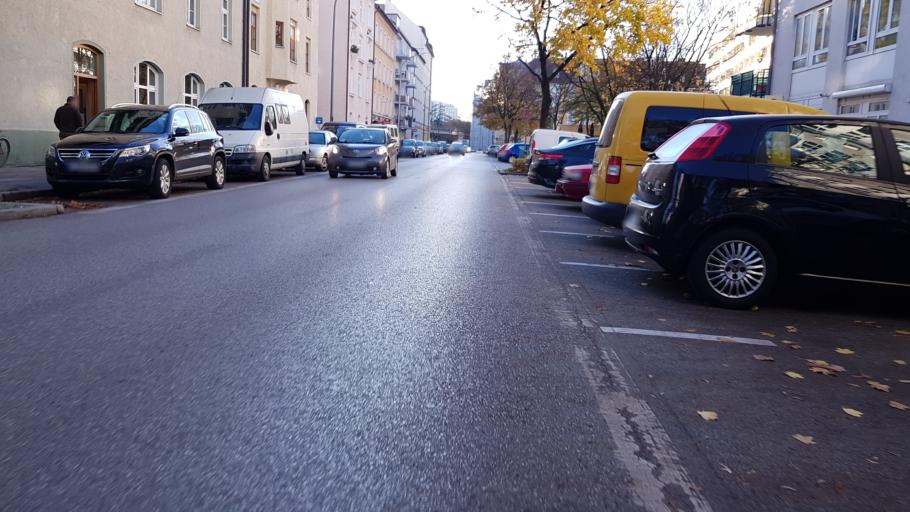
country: DE
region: Bavaria
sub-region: Upper Bavaria
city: Munich
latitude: 48.1252
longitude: 11.5960
